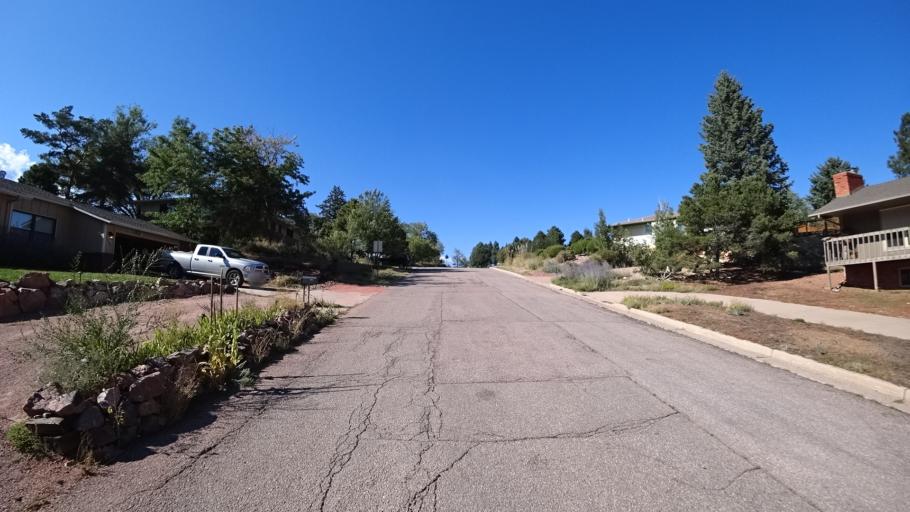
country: US
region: Colorado
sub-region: El Paso County
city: Colorado Springs
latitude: 38.8519
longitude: -104.8389
